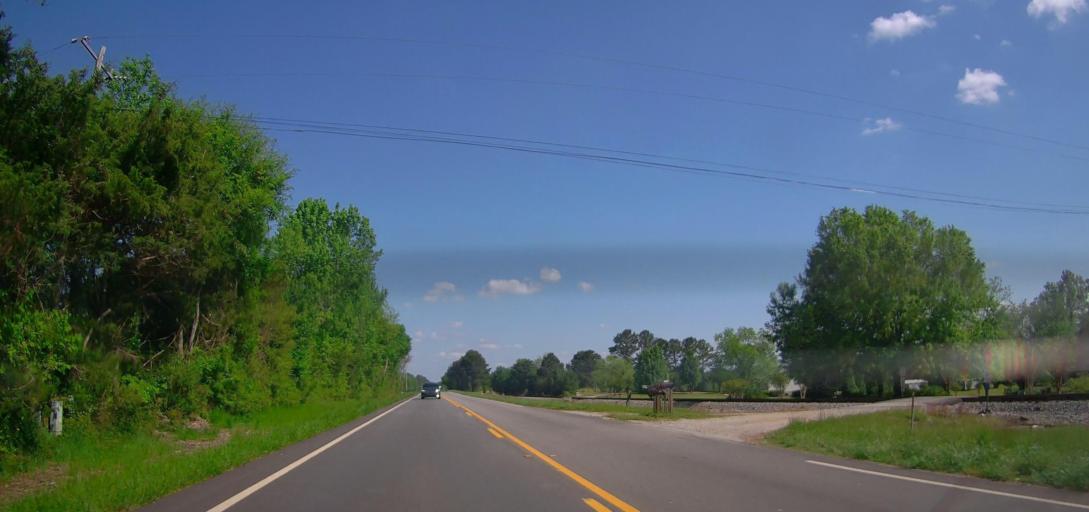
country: US
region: Georgia
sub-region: Morgan County
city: Madison
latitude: 33.6081
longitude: -83.4317
